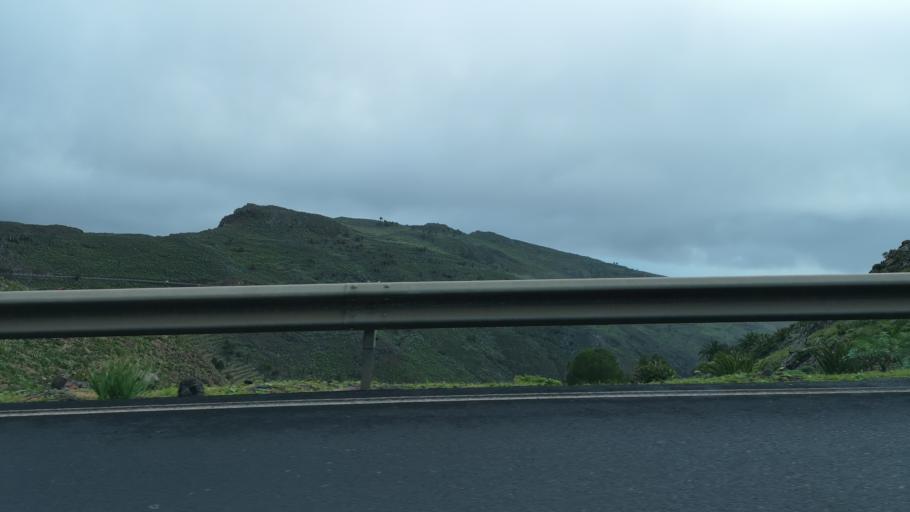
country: ES
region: Canary Islands
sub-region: Provincia de Santa Cruz de Tenerife
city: San Sebastian de la Gomera
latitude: 28.0979
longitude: -17.1735
